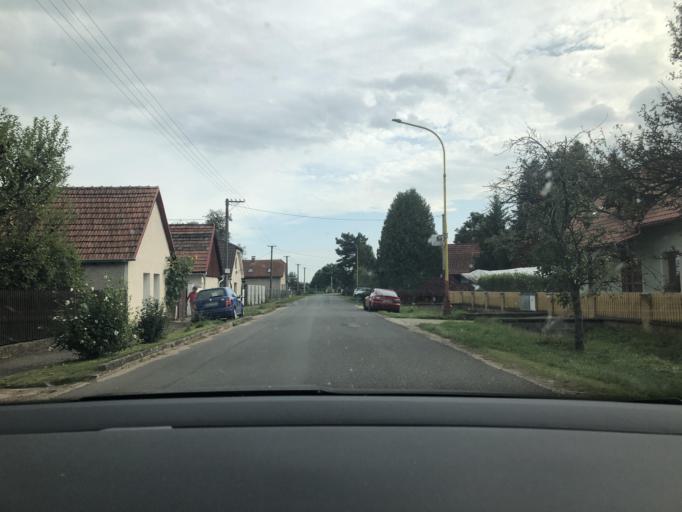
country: CZ
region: Pardubicky
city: Chvaletice
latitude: 50.0918
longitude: 15.4416
